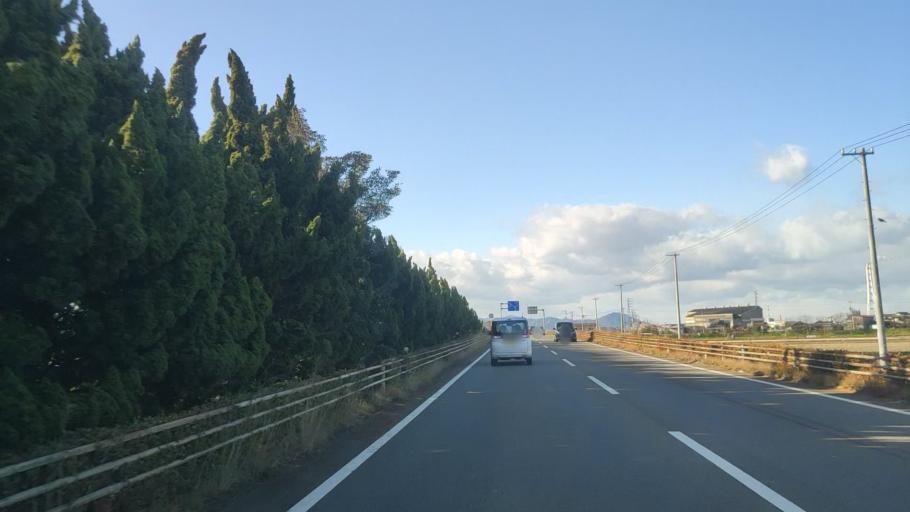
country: JP
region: Ehime
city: Saijo
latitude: 33.9172
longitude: 133.1280
